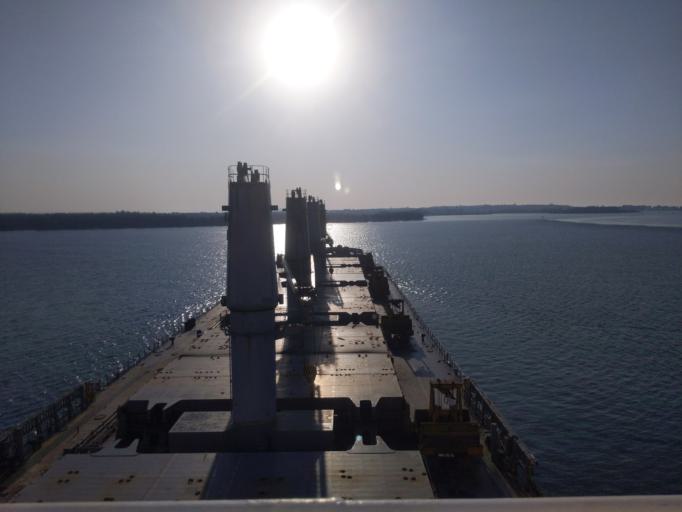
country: ZA
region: KwaZulu-Natal
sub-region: uThungulu District Municipality
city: Richards Bay
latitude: -28.8022
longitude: 32.0547
